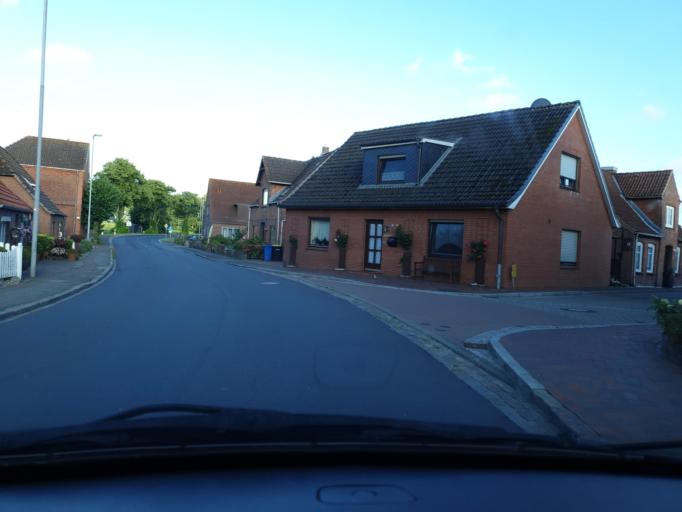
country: DE
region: Schleswig-Holstein
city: Wohrden
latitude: 54.1654
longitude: 9.0002
